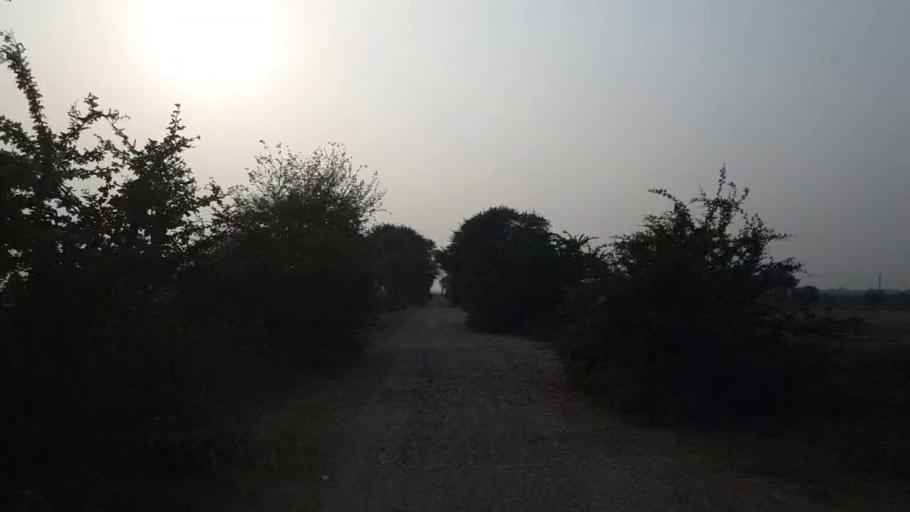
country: PK
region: Sindh
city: Mirpur Batoro
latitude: 24.6605
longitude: 68.3777
